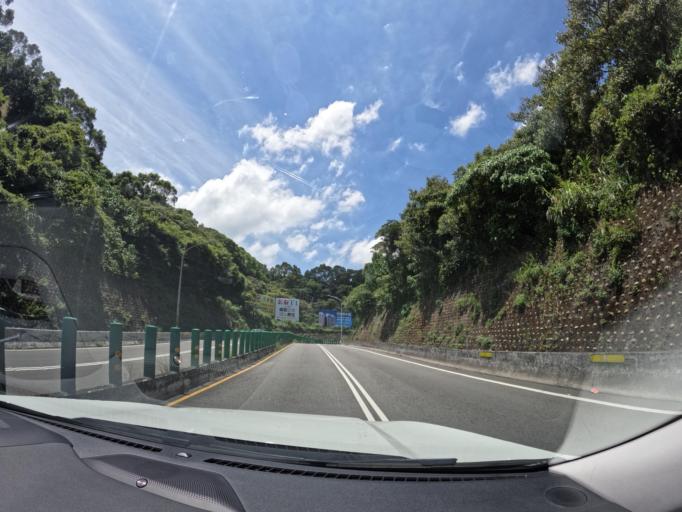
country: TW
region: Taipei
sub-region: Taipei
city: Banqiao
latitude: 25.0370
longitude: 121.3874
